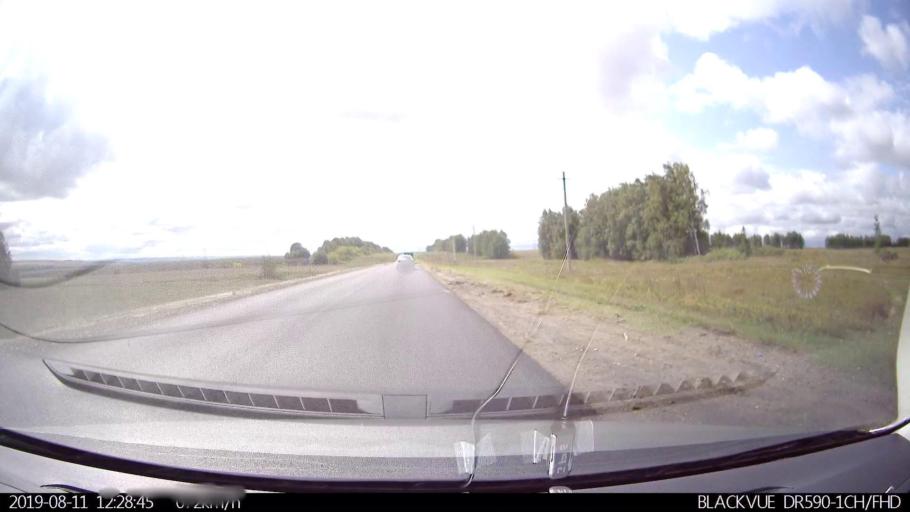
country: RU
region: Ulyanovsk
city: Ignatovka
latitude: 53.8406
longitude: 47.9089
